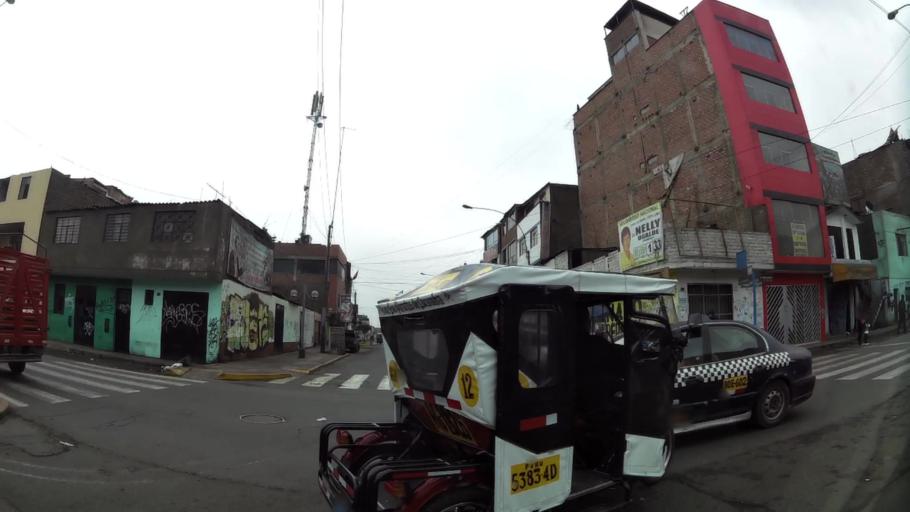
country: PE
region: Lima
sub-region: Lima
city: San Luis
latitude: -12.0520
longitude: -77.0033
